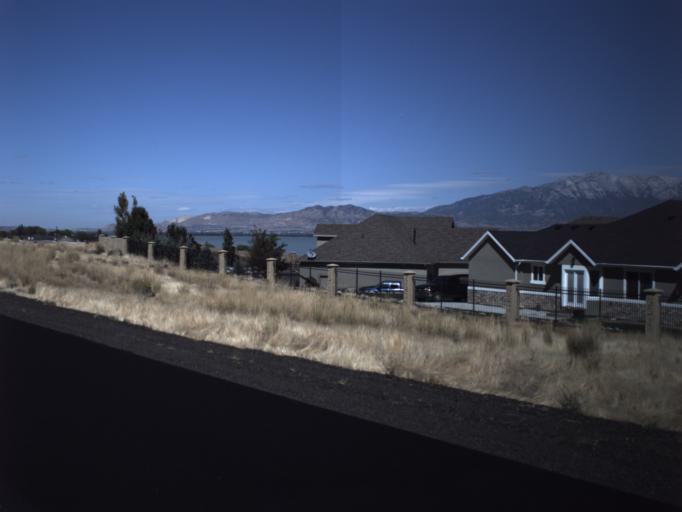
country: US
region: Utah
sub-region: Utah County
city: Saratoga Springs
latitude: 40.2918
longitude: -111.8795
